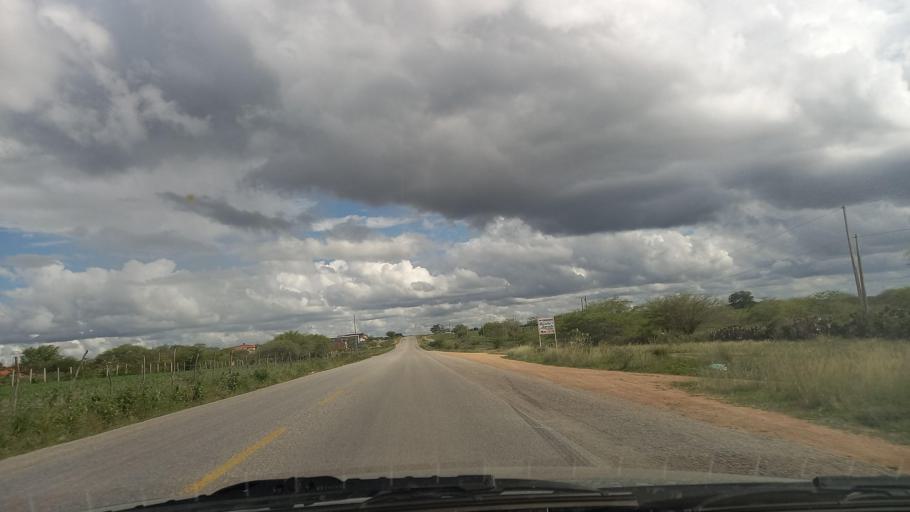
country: BR
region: Pernambuco
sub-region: Cachoeirinha
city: Cachoeirinha
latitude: -8.5044
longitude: -36.2484
